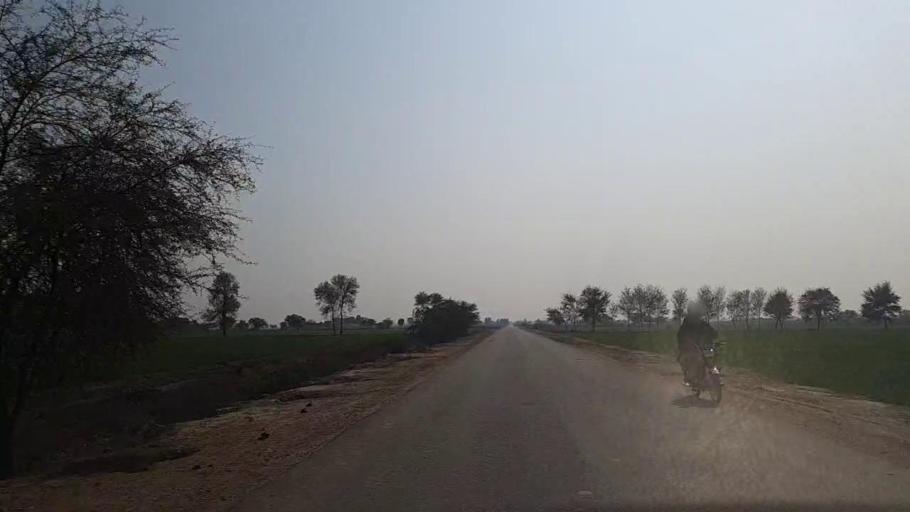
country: PK
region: Sindh
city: Jam Sahib
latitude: 26.3596
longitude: 68.5347
